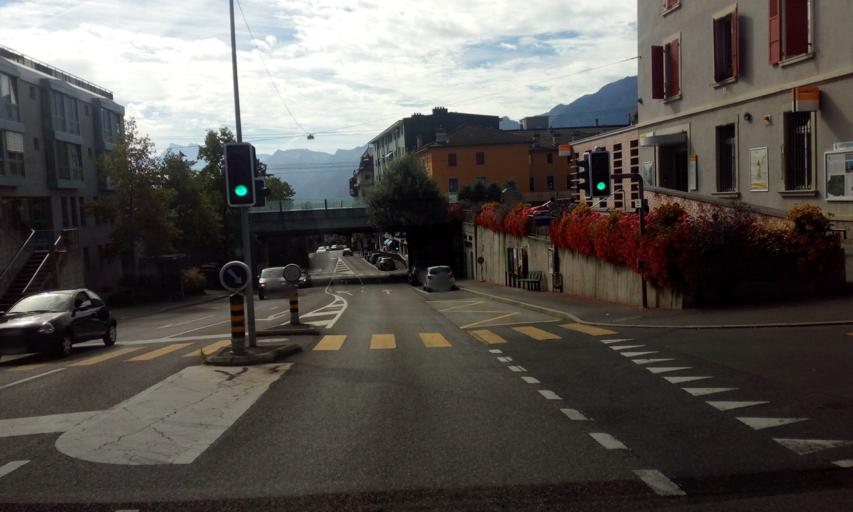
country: CH
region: Vaud
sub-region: Riviera-Pays-d'Enhaut District
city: Le Chatelard
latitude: 46.4436
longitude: 6.8965
